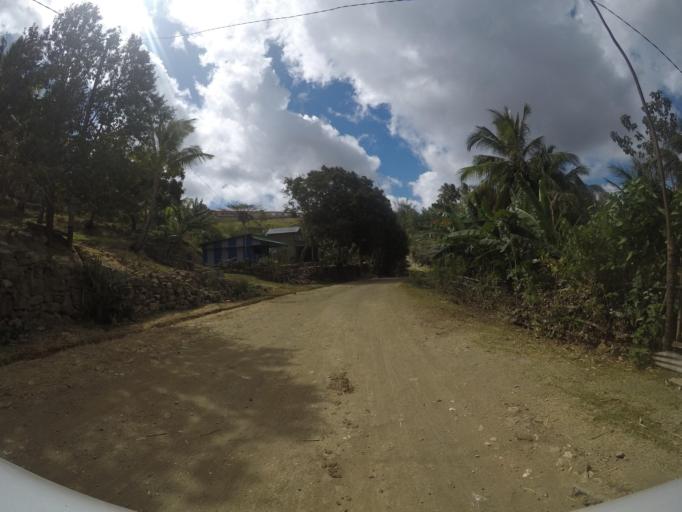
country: TL
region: Lautem
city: Lospalos
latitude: -8.5435
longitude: 126.8358
